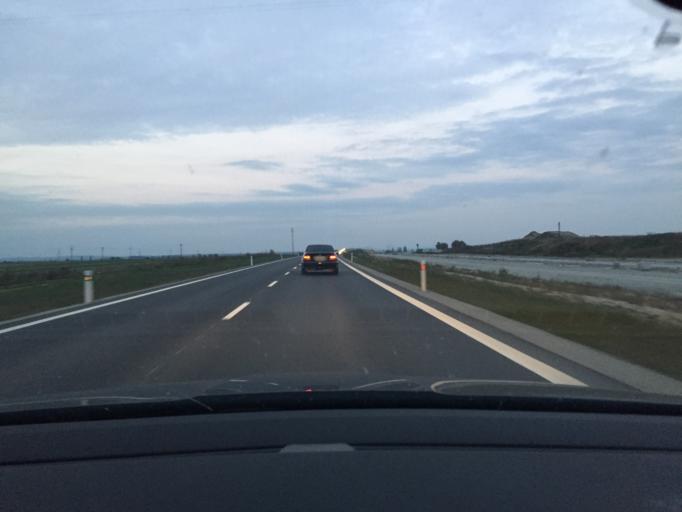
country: CZ
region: Jihocesky
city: Dolni Bukovsko
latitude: 49.1487
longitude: 14.6267
